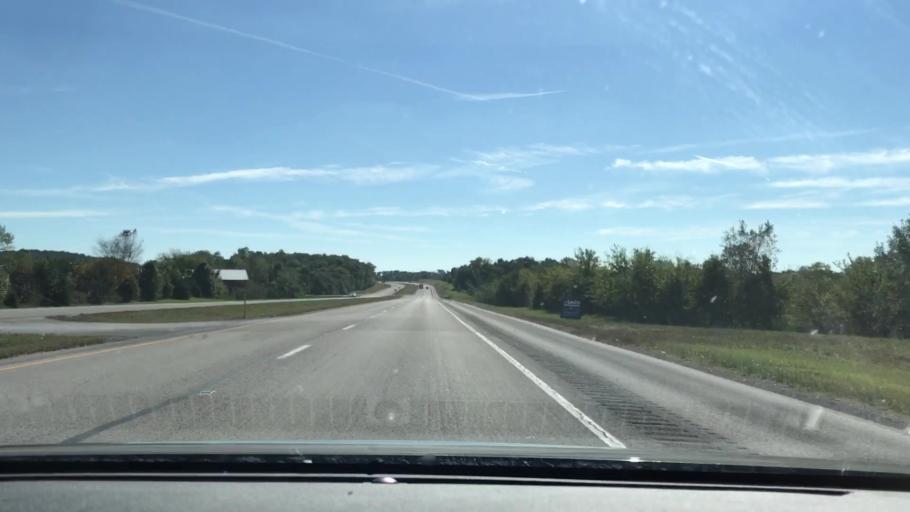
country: US
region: Kentucky
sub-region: Todd County
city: Elkton
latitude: 36.8319
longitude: -87.2301
